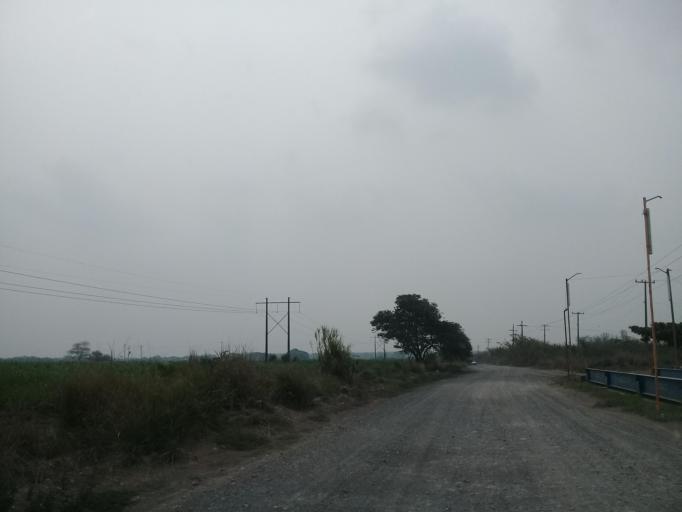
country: MX
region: Veracruz
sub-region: Medellin
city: La Laguna y Monte del Castillo
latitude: 18.9093
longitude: -96.1934
